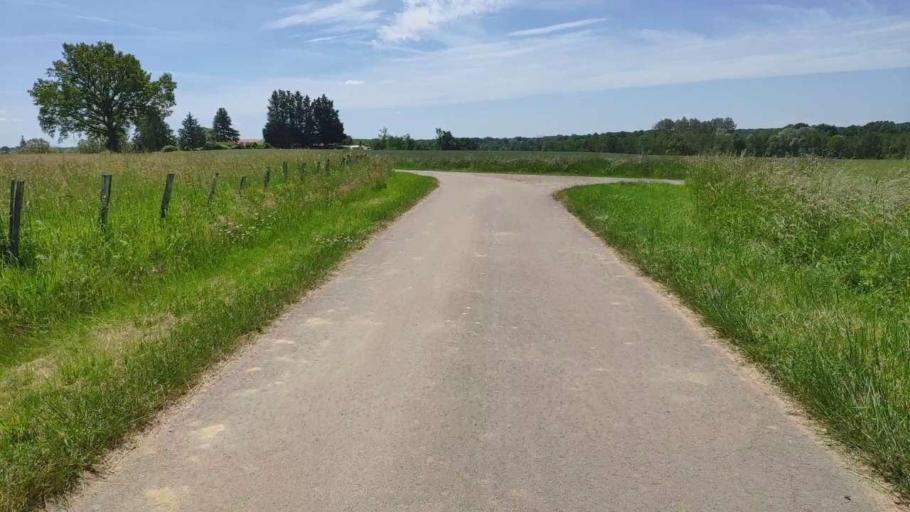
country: FR
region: Franche-Comte
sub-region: Departement du Jura
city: Bletterans
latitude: 46.7952
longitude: 5.3915
